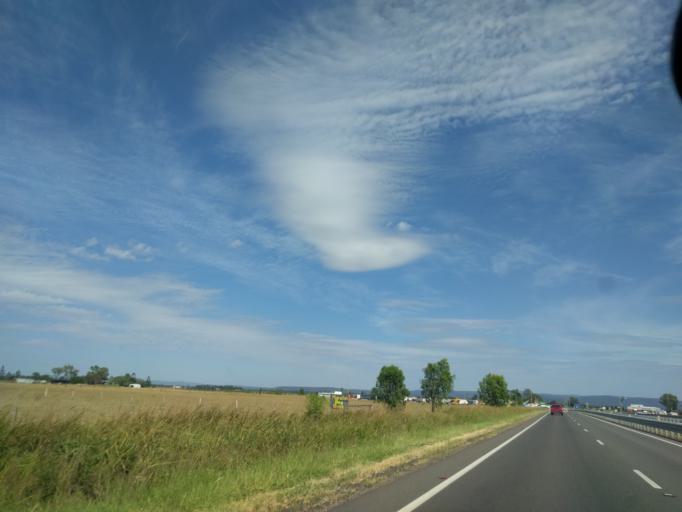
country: AU
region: Queensland
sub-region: Lockyer Valley
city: Gatton
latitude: -27.5471
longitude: 152.3820
